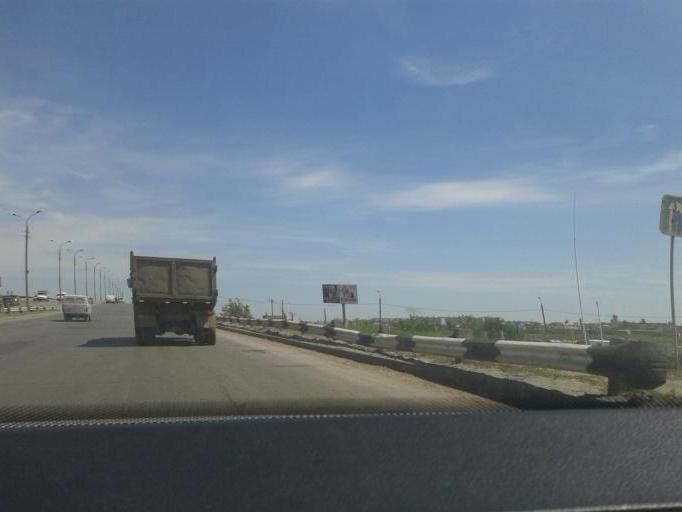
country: RU
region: Volgograd
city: Volgograd
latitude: 48.7644
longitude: 44.5147
